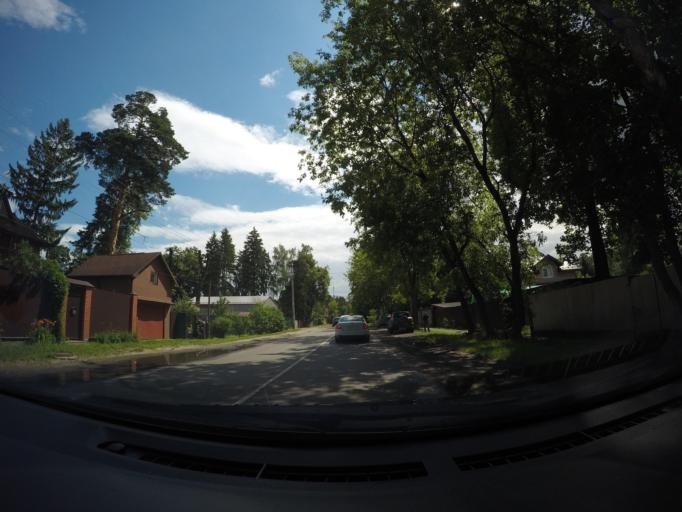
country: RU
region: Moskovskaya
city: Kraskovo
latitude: 55.6557
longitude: 37.9896
